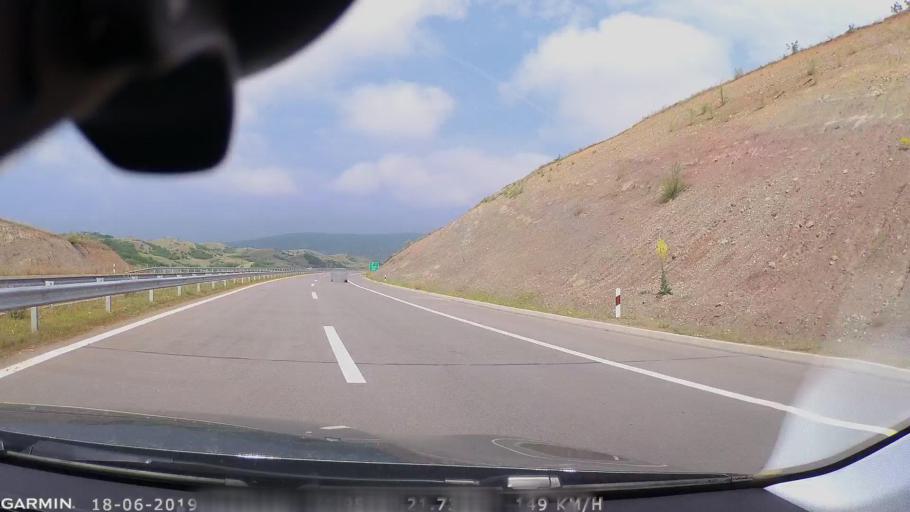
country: MK
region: Sveti Nikole
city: Gorobinci
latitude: 41.9278
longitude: 21.8315
